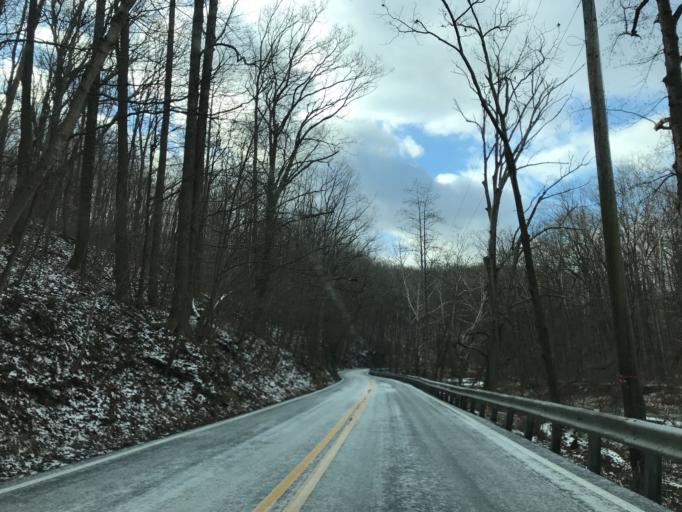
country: US
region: Maryland
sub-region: Harford County
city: Jarrettsville
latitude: 39.6299
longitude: -76.4013
